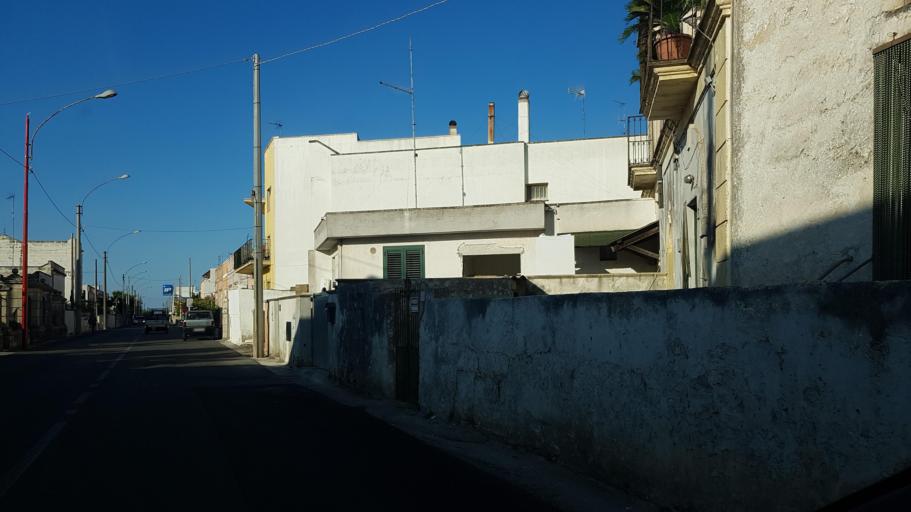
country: IT
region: Apulia
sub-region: Provincia di Lecce
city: Andrano
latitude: 39.9879
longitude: 18.3820
